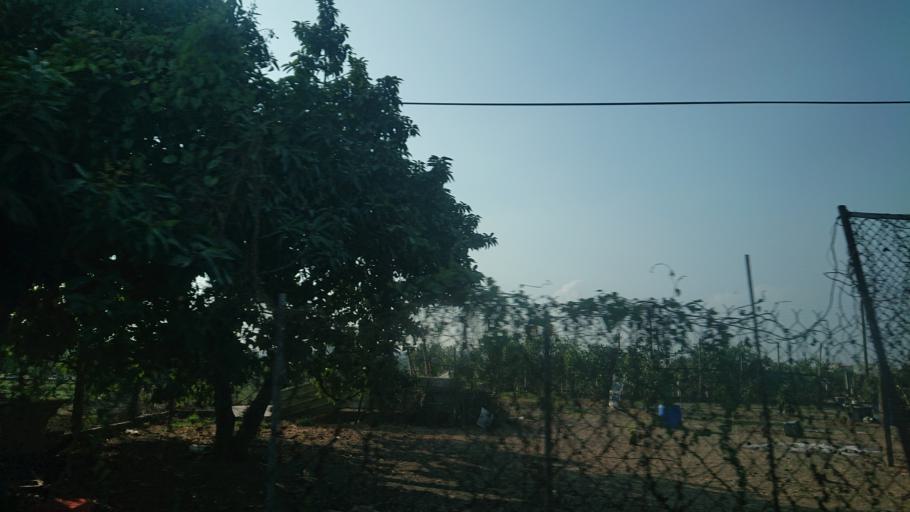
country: TW
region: Taiwan
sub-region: Tainan
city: Tainan
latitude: 23.1514
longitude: 120.2485
